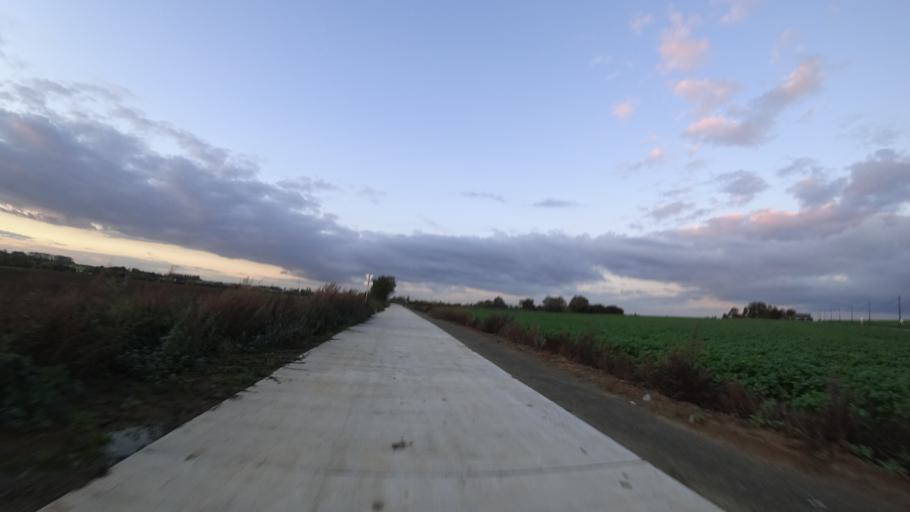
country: BE
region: Wallonia
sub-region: Province de Namur
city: Gembloux
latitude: 50.5672
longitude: 4.7136
